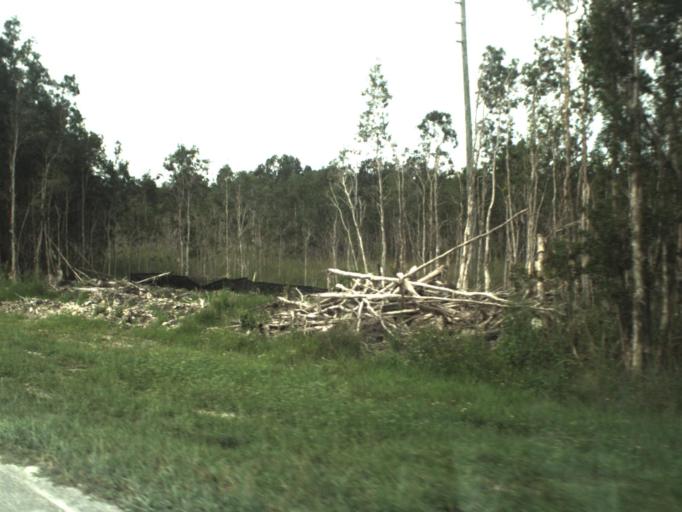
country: US
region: Florida
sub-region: Miami-Dade County
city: Kendall West
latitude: 25.7571
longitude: -80.4813
